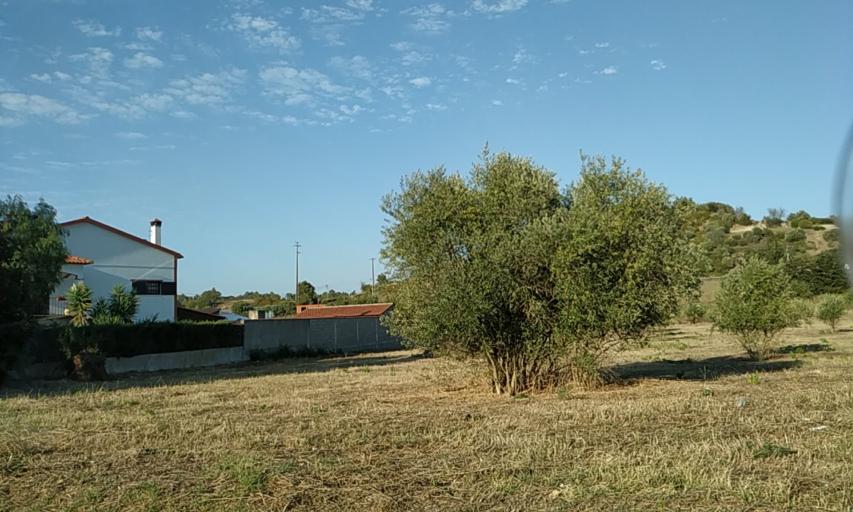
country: PT
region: Santarem
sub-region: Alcanena
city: Alcanena
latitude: 39.3765
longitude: -8.6610
